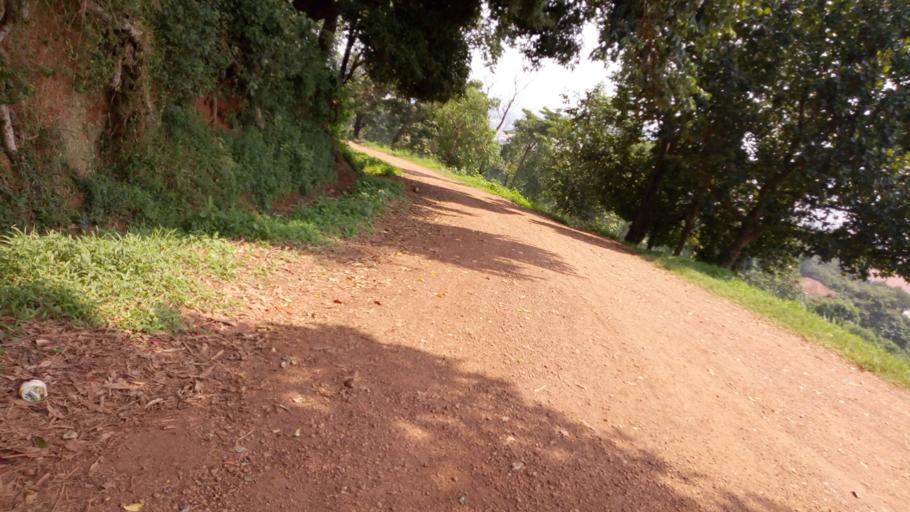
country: UG
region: Central Region
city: Kampala Central Division
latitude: 0.3400
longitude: 32.5648
